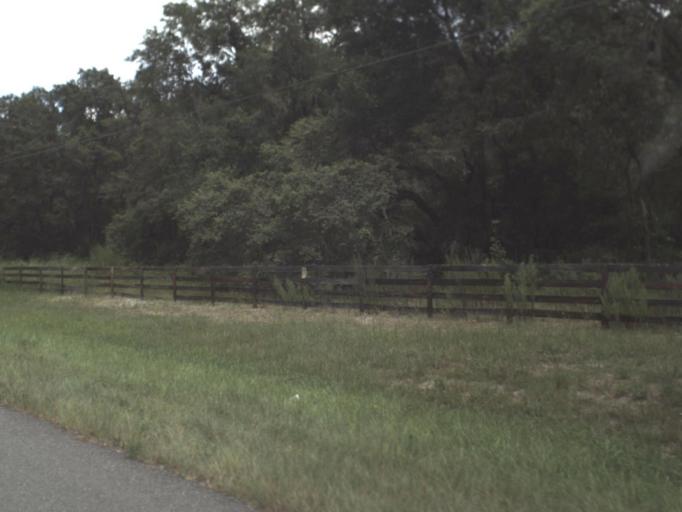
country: US
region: Florida
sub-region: Hernando County
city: Ridge Manor
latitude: 28.5314
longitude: -82.1646
